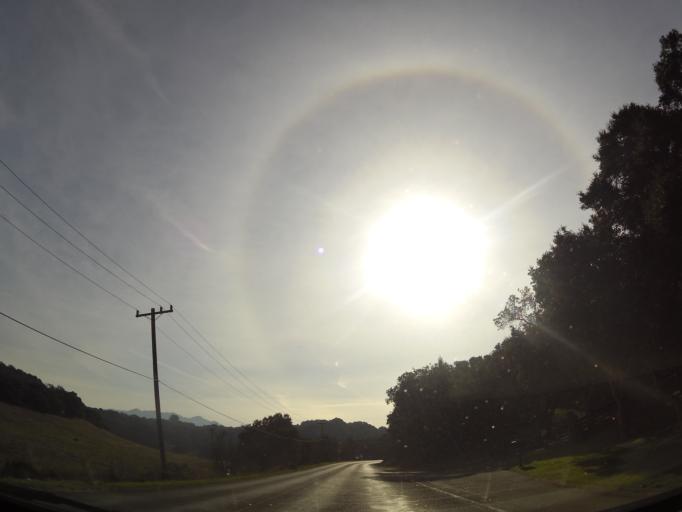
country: US
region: California
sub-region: Monterey County
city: Prunedale
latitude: 36.7922
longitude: -121.6132
